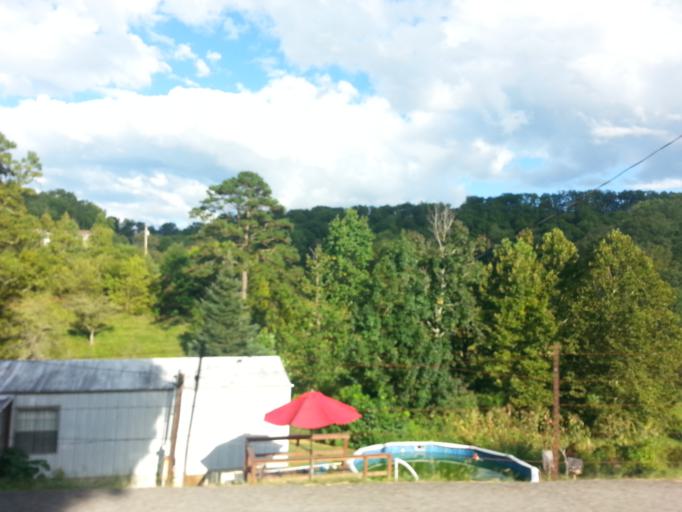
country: US
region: Tennessee
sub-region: Knox County
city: Mascot
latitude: 36.1135
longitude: -83.7506
